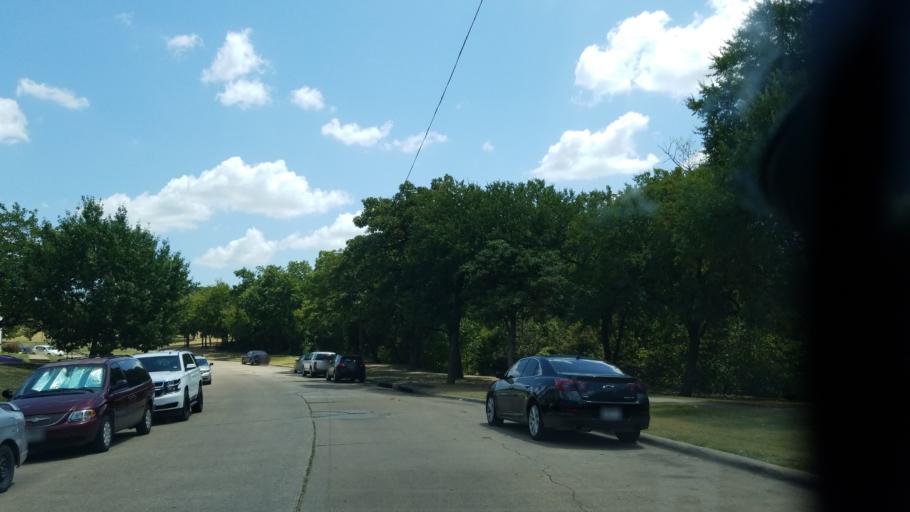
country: US
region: Texas
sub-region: Dallas County
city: Cockrell Hill
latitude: 32.7329
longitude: -96.9226
